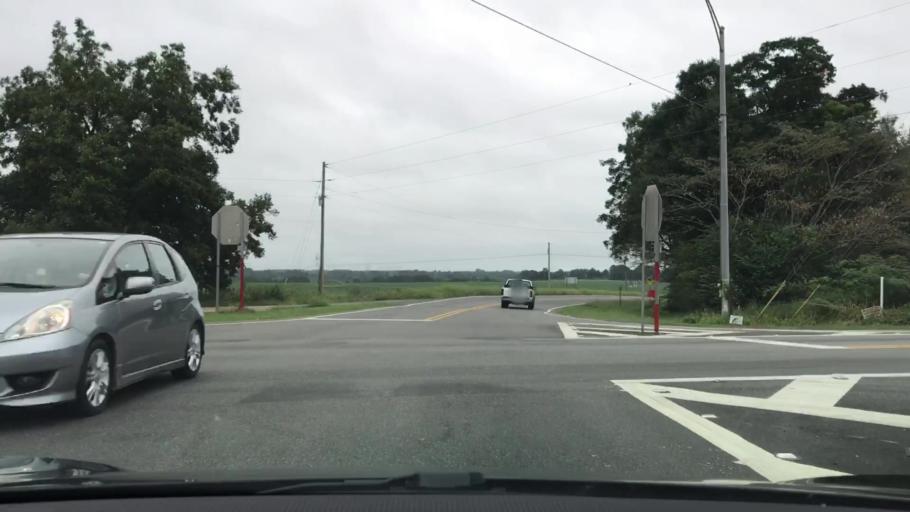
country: US
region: Alabama
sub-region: Covington County
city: Opp
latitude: 31.2804
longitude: -86.1571
